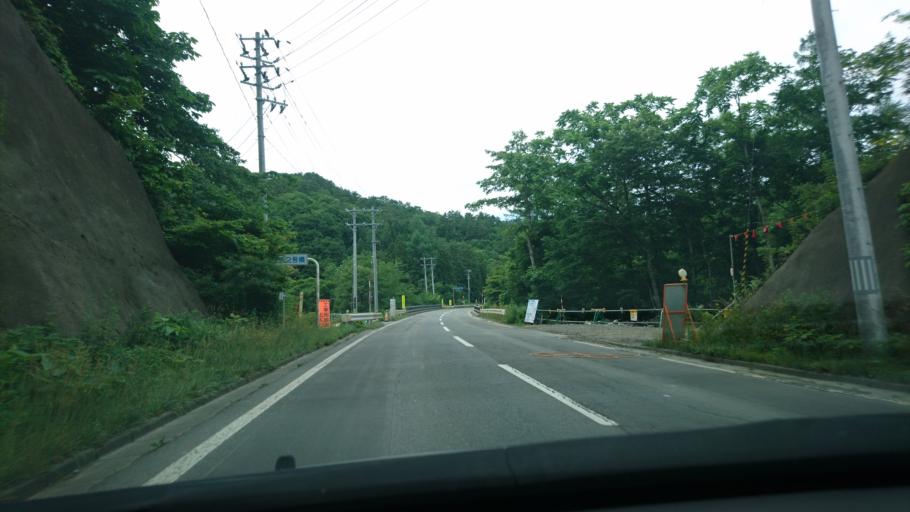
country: JP
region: Iwate
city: Miyako
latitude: 39.9770
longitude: 141.8575
